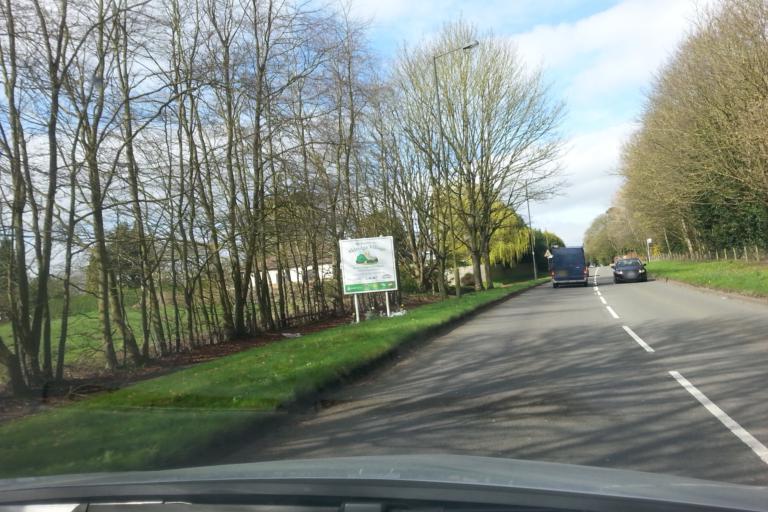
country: GB
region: England
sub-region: Walsall
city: Aldridge
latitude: 52.6024
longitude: -1.9058
